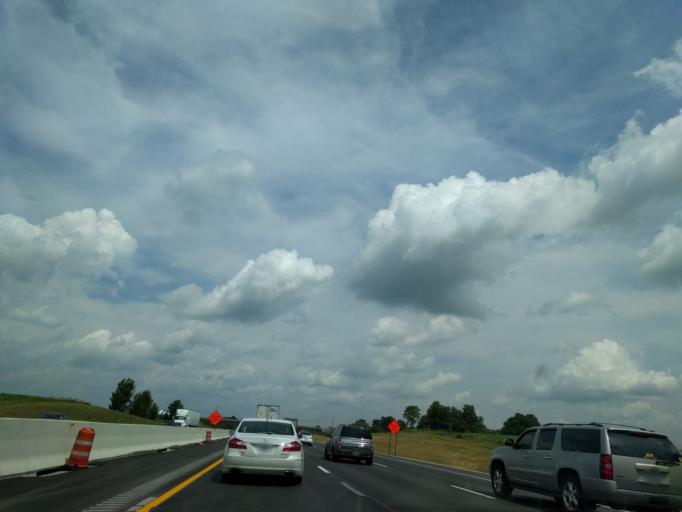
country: US
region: Kentucky
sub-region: Larue County
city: Hodgenville
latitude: 37.5357
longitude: -85.8818
